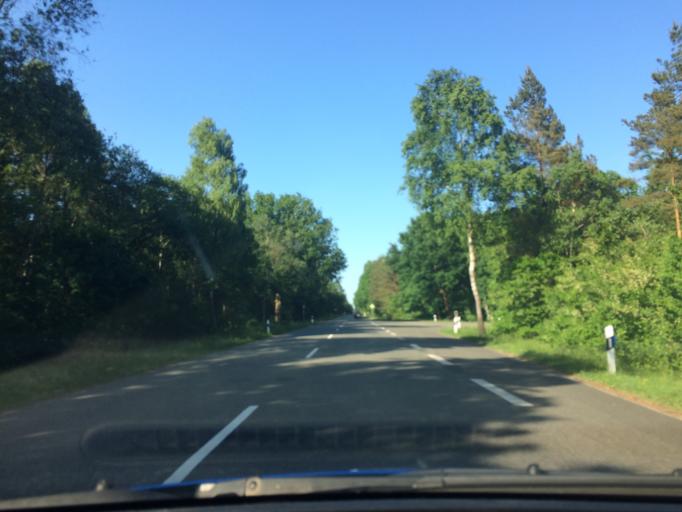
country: DE
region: Lower Saxony
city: Bispingen
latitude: 53.0626
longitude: 9.9592
